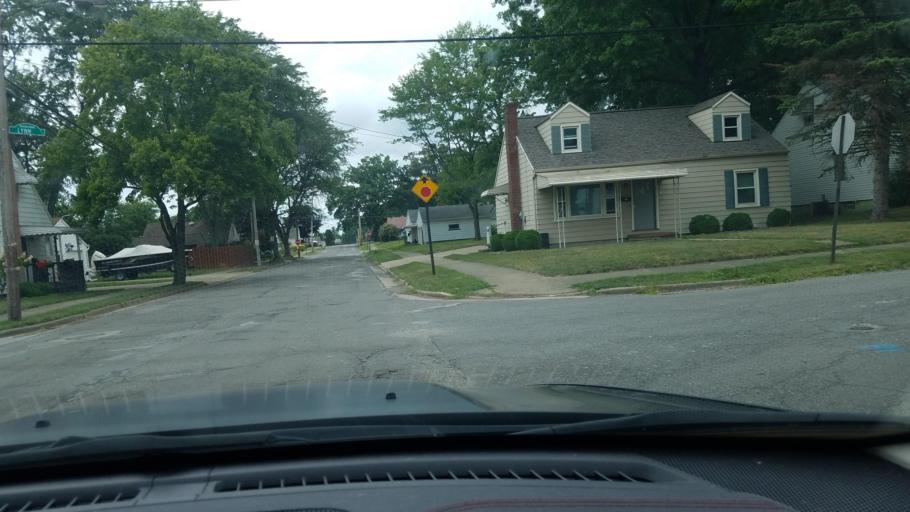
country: US
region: Ohio
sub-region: Mahoning County
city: Struthers
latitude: 41.0518
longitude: -80.6259
